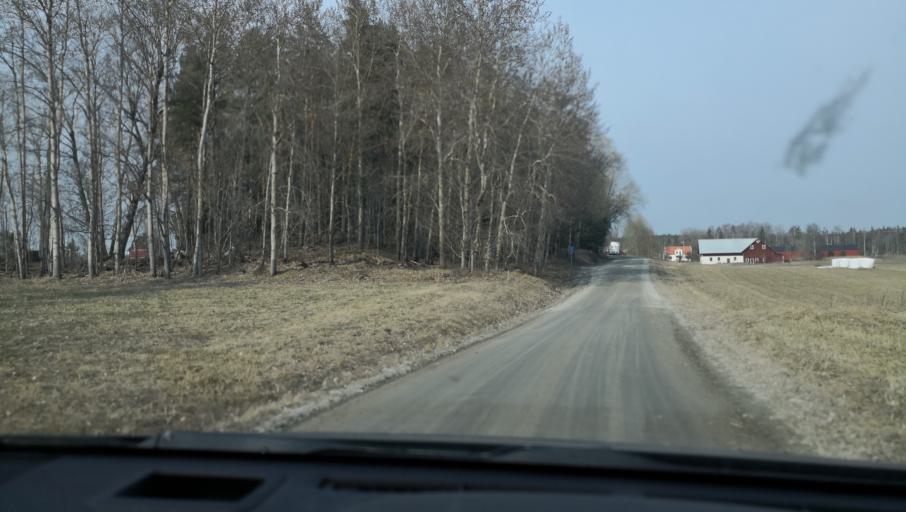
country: SE
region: OErebro
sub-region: Lindesbergs Kommun
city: Frovi
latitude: 59.3482
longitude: 15.4387
